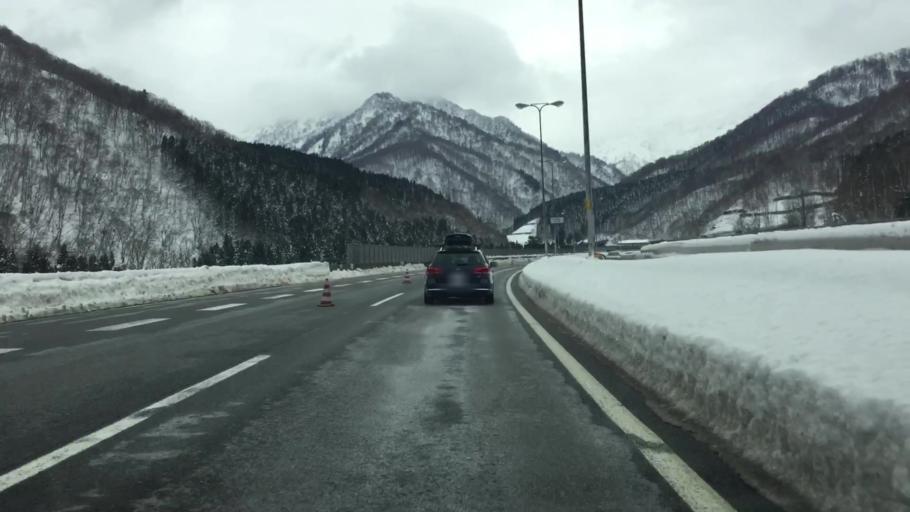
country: JP
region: Niigata
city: Shiozawa
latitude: 36.8751
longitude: 138.8628
